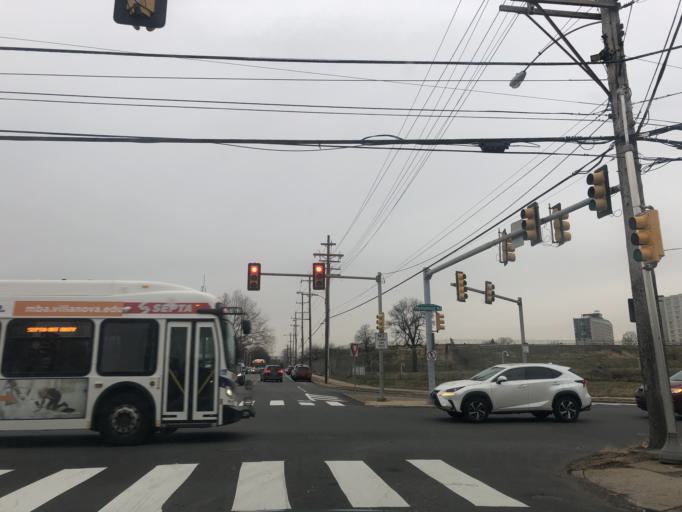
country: US
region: Pennsylvania
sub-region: Montgomery County
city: Bala-Cynwyd
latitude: 40.0011
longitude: -75.2152
